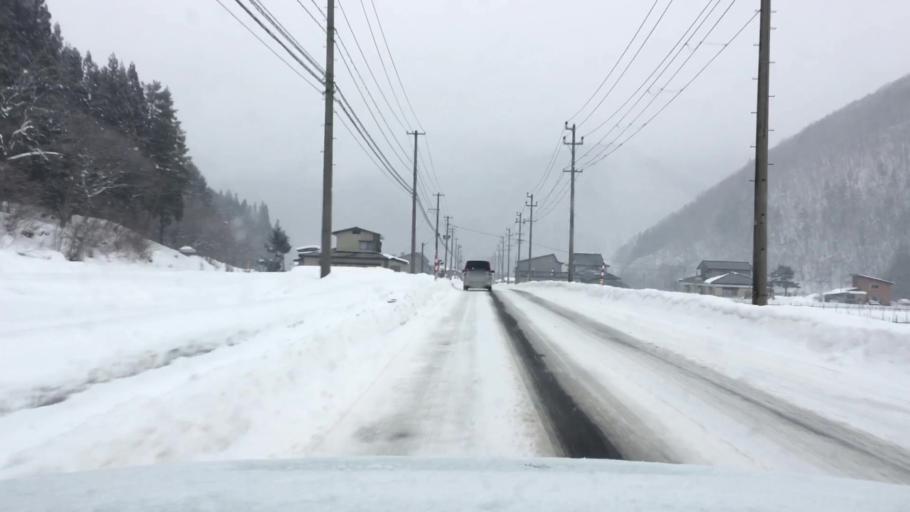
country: JP
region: Akita
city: Hanawa
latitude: 40.0733
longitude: 141.0197
